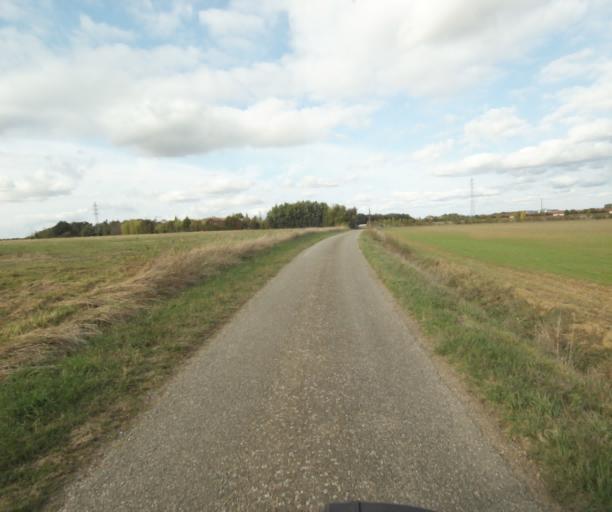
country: FR
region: Midi-Pyrenees
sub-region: Departement du Tarn-et-Garonne
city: Verdun-sur-Garonne
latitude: 43.8399
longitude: 1.1606
